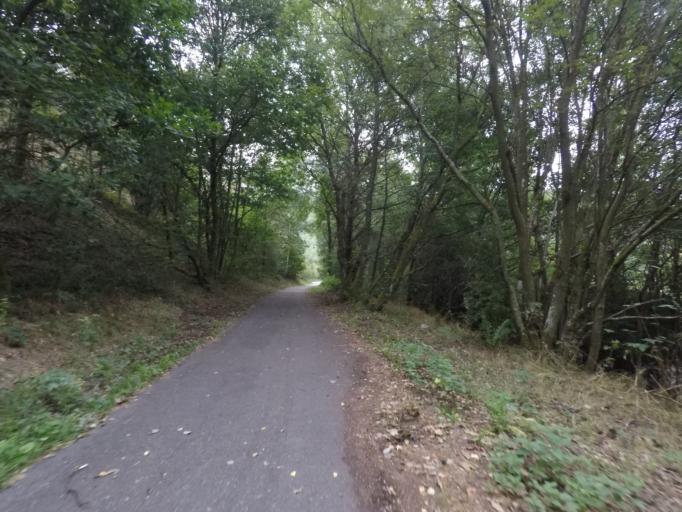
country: BE
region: Wallonia
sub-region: Province du Luxembourg
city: Martelange
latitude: 49.8440
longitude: 5.7258
